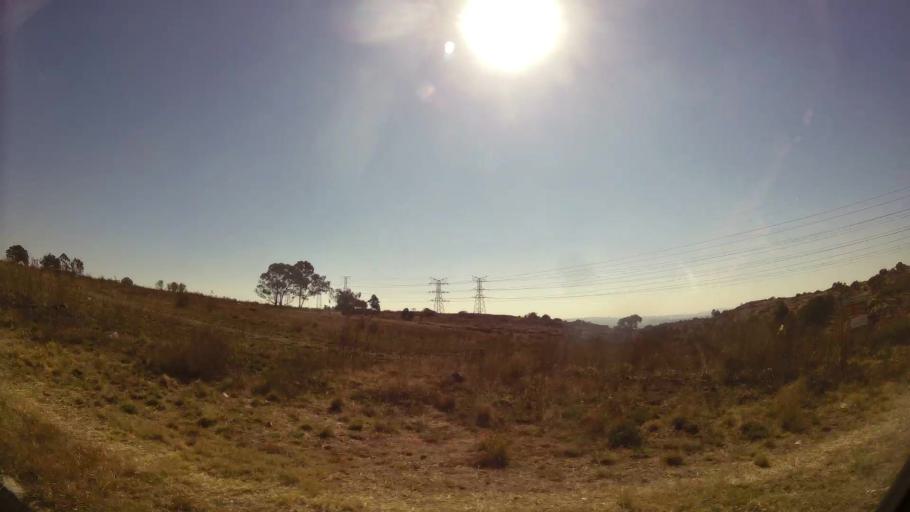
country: ZA
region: Gauteng
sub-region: City of Johannesburg Metropolitan Municipality
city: Johannesburg
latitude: -26.2580
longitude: 28.0718
